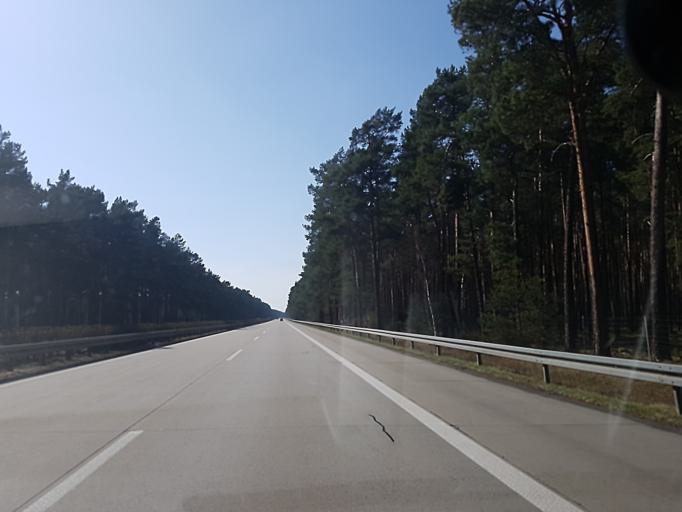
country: DE
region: Brandenburg
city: Forst
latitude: 51.7089
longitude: 14.5389
